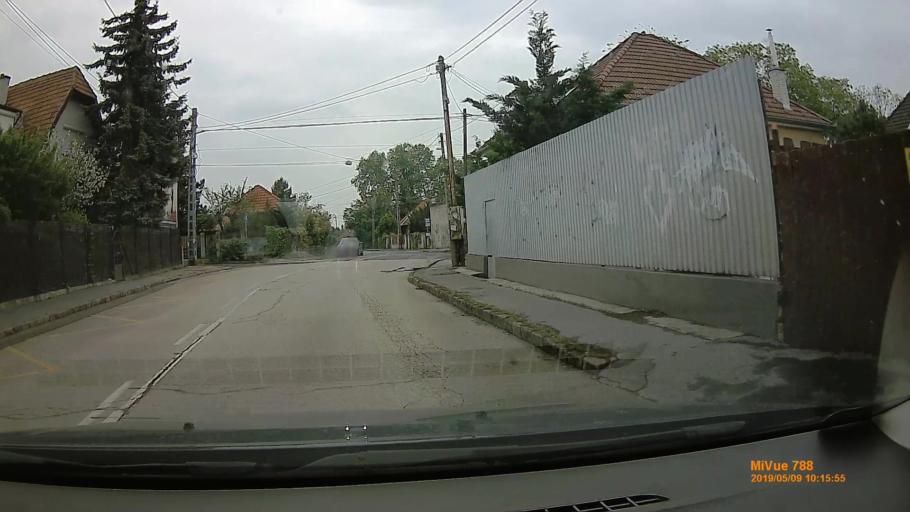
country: HU
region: Budapest
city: Budapest XVI. keruelet
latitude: 47.5154
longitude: 19.1637
